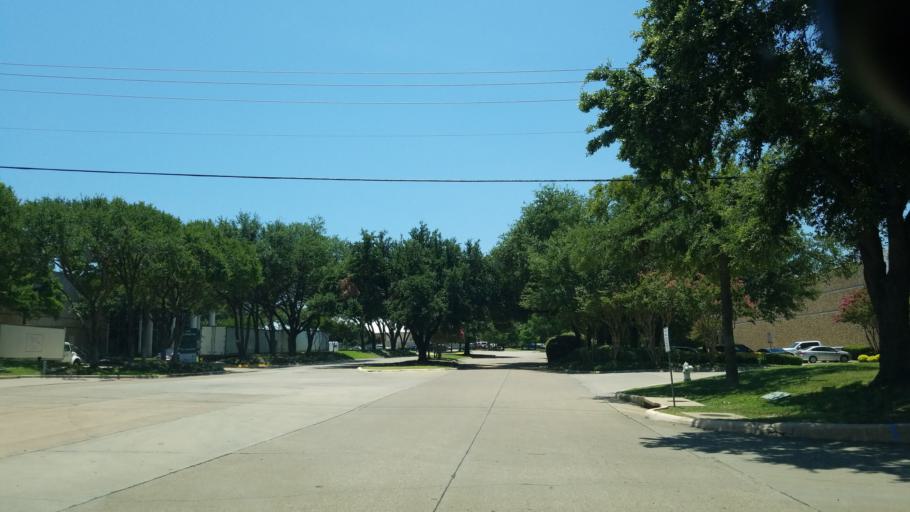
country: US
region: Texas
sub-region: Dallas County
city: Farmers Branch
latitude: 32.9310
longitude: -96.9068
